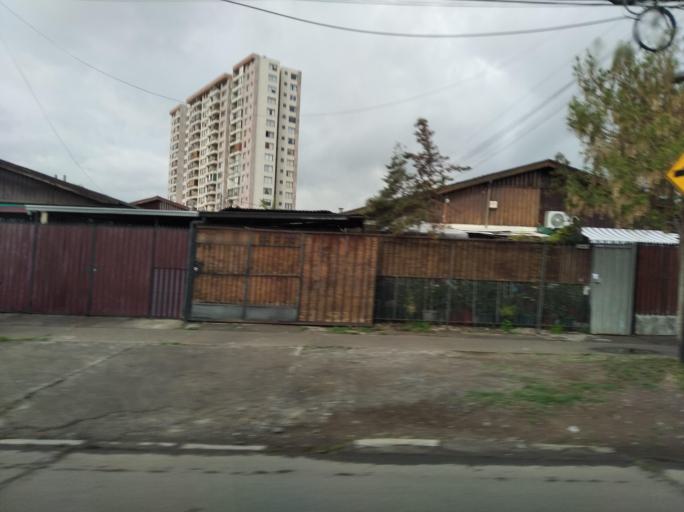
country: CL
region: Santiago Metropolitan
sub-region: Provincia de Santiago
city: Villa Presidente Frei, Nunoa, Santiago, Chile
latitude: -33.4974
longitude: -70.6000
